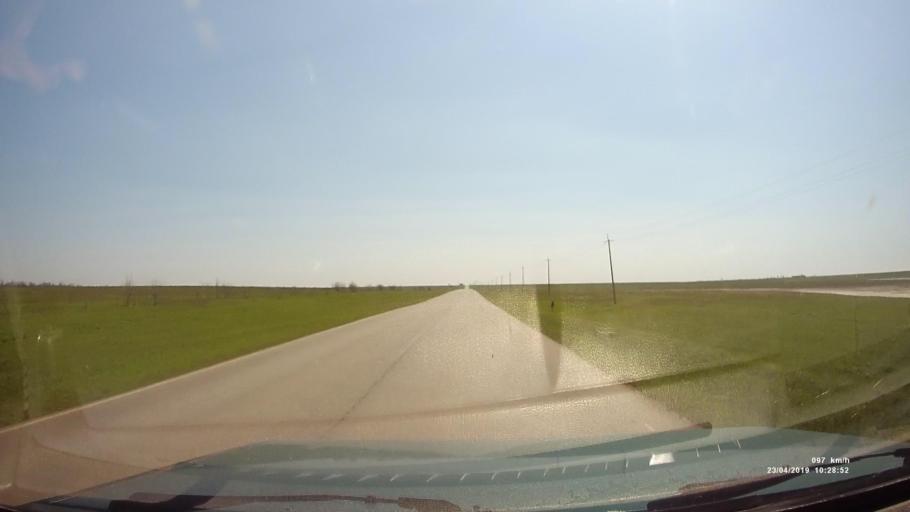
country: RU
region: Kalmykiya
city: Yashalta
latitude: 46.6023
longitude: 42.5158
